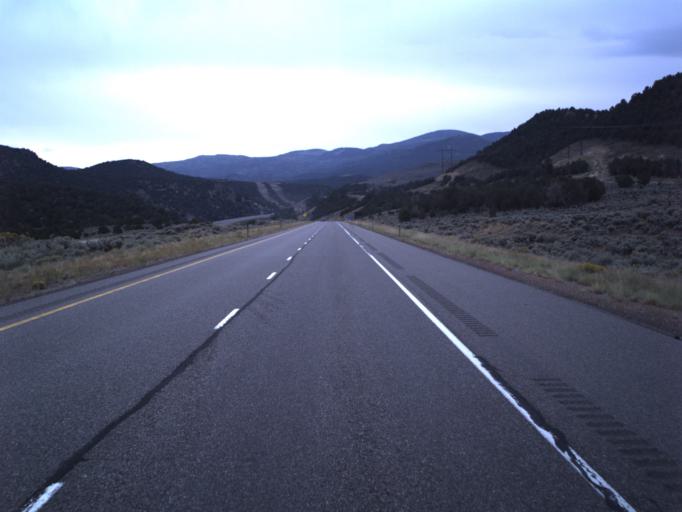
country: US
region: Utah
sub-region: Sevier County
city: Monroe
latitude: 38.5685
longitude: -112.4471
